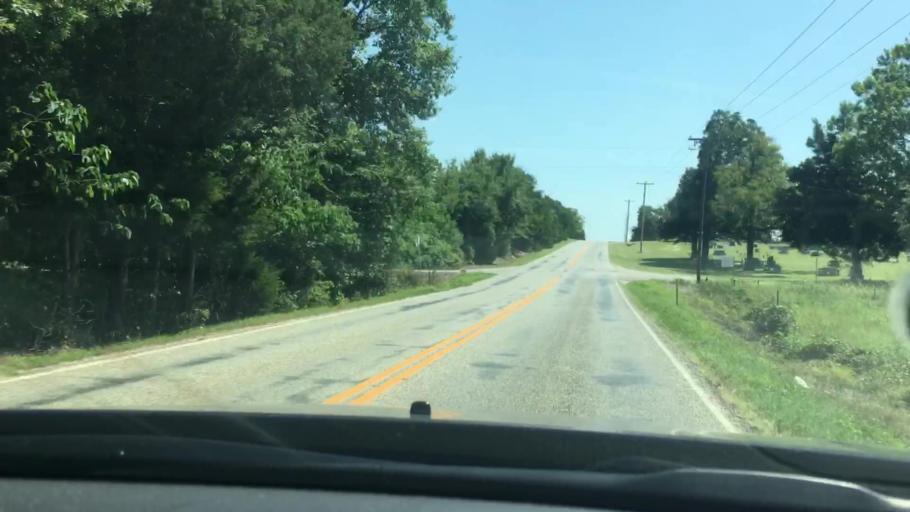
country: US
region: Oklahoma
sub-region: Johnston County
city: Tishomingo
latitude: 34.2377
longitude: -96.5845
